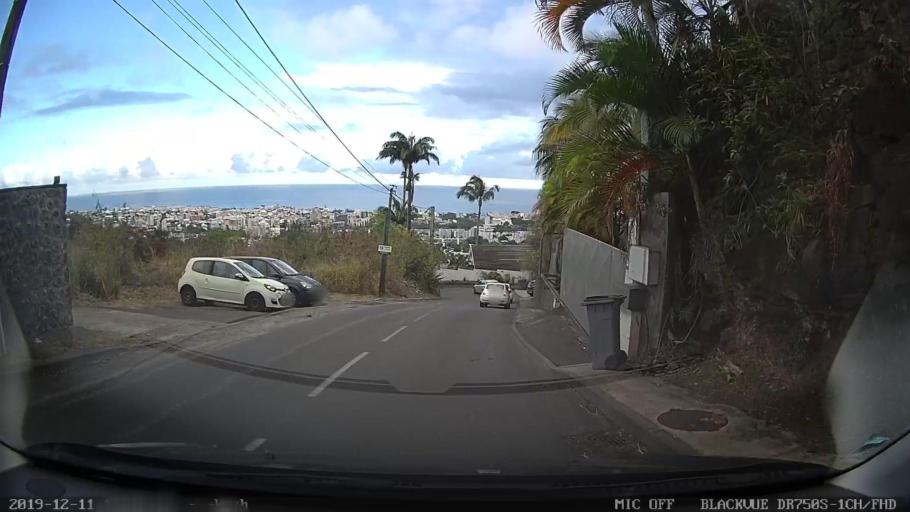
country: RE
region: Reunion
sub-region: Reunion
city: Saint-Denis
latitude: -20.9034
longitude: 55.4583
